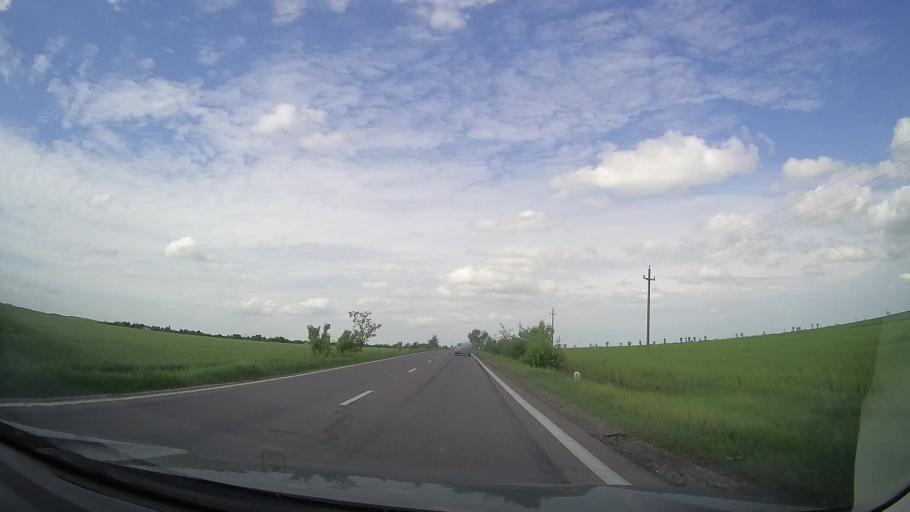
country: RO
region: Giurgiu
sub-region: Comuna Rasuceni
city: Rasuceni
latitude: 44.1315
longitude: 25.6971
